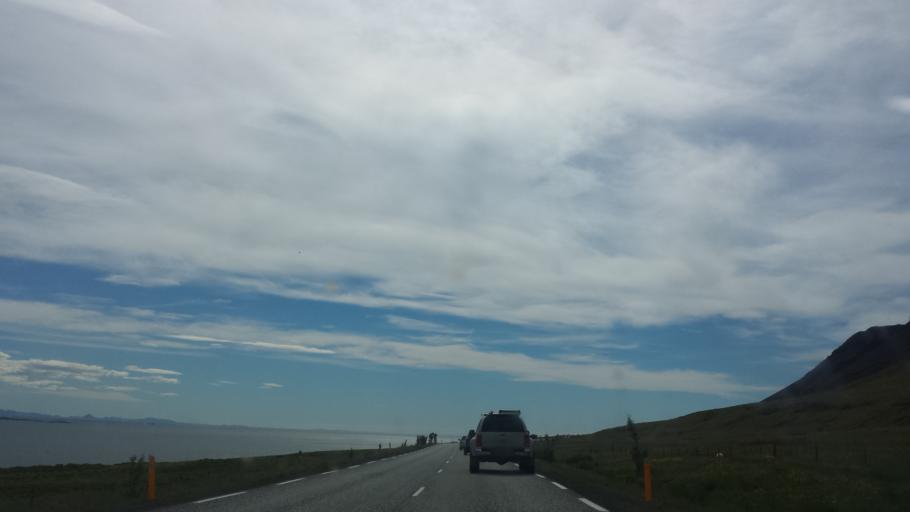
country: IS
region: Capital Region
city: Reykjavik
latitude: 64.3347
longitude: -21.8395
